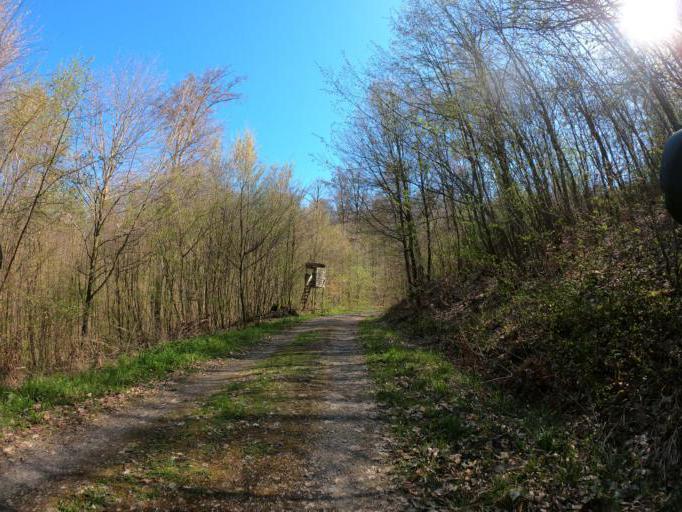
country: DE
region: Baden-Wuerttemberg
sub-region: Karlsruhe Region
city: Illingen
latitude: 48.9064
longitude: 8.9052
